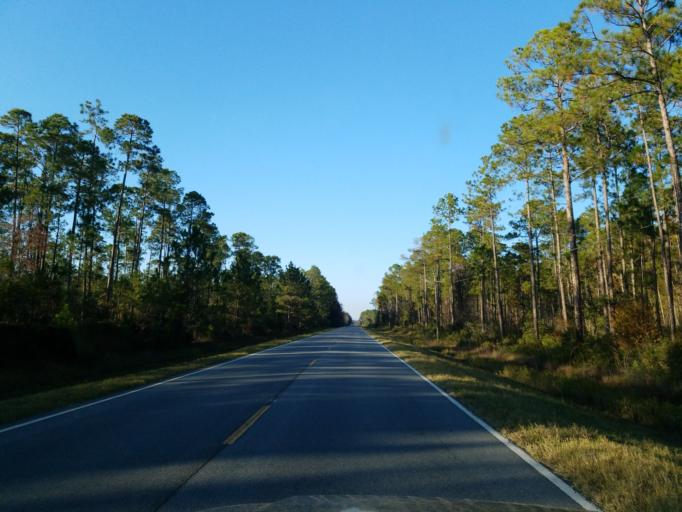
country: US
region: Georgia
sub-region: Lanier County
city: Lakeland
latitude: 31.1064
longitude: -83.0806
